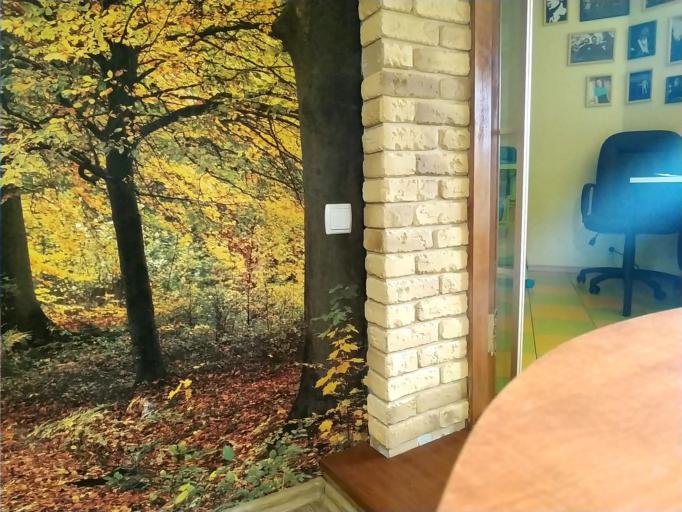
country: BY
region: Mogilev
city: Khotsimsk
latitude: 53.5648
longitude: 32.5377
